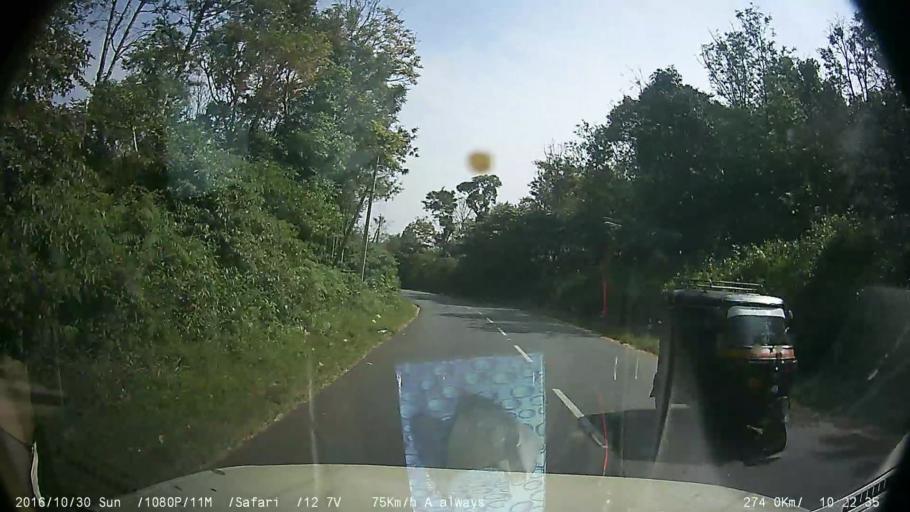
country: IN
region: Karnataka
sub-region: Kodagu
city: Madikeri
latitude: 12.4294
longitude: 75.7656
